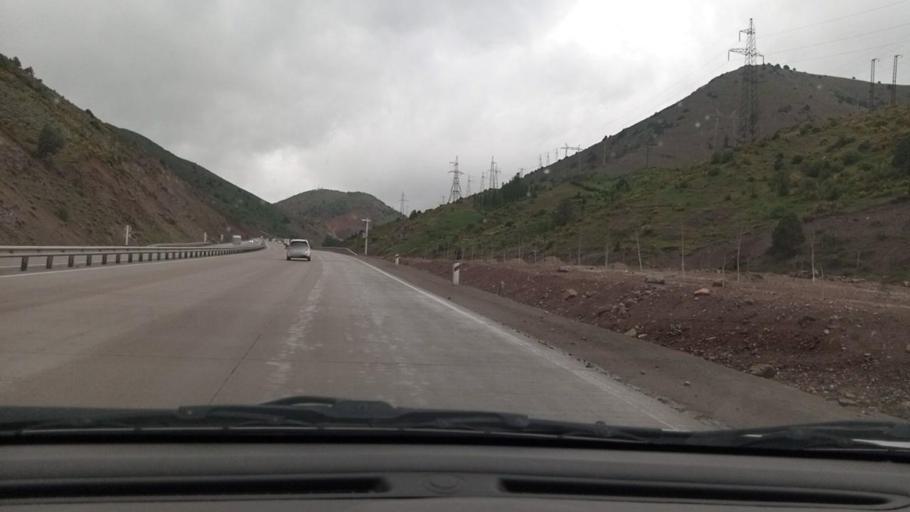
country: UZ
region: Toshkent
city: Angren
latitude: 41.0529
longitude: 70.5667
